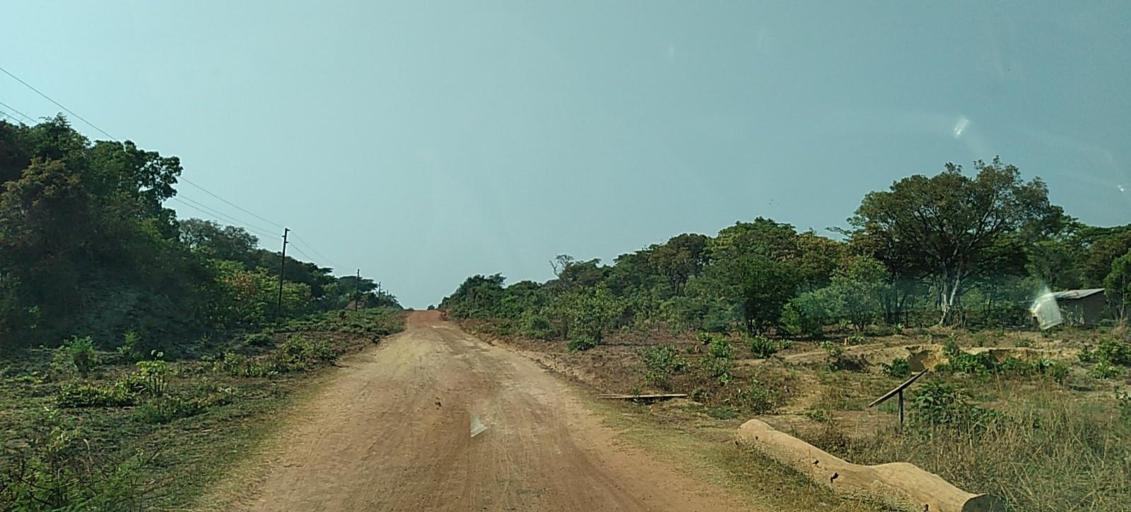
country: ZM
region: Copperbelt
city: Chingola
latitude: -12.9090
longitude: 27.3718
